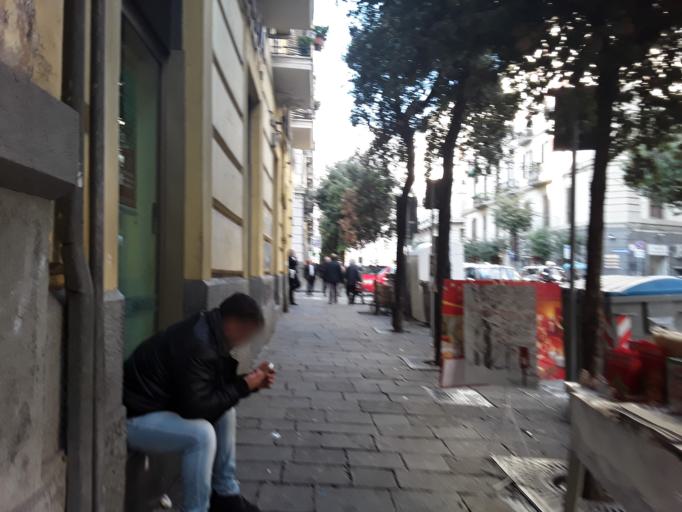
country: IT
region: Campania
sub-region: Provincia di Napoli
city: Napoli
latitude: 40.8609
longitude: 14.2666
